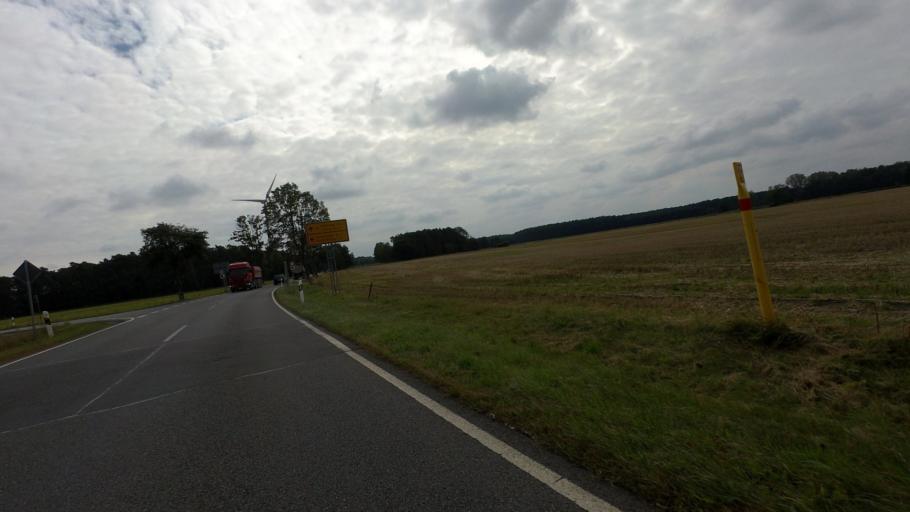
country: DE
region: Brandenburg
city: Kasel-Golzig
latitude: 51.9354
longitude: 13.6623
